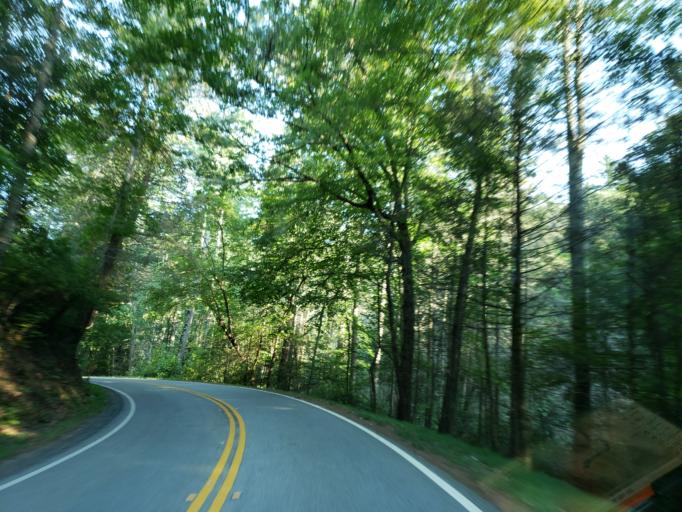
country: US
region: Georgia
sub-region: Union County
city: Blairsville
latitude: 34.7392
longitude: -84.0852
